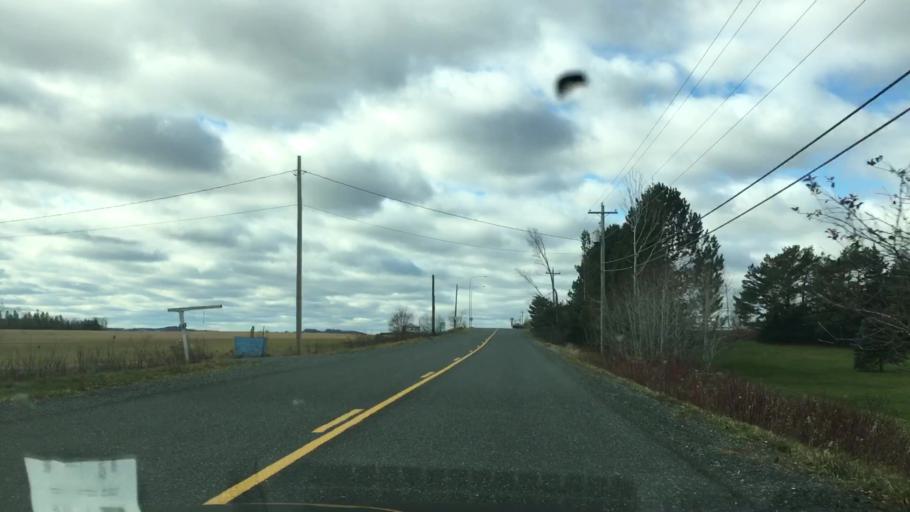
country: CA
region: New Brunswick
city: Florenceville-Bristol
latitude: 46.2879
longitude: -67.5465
